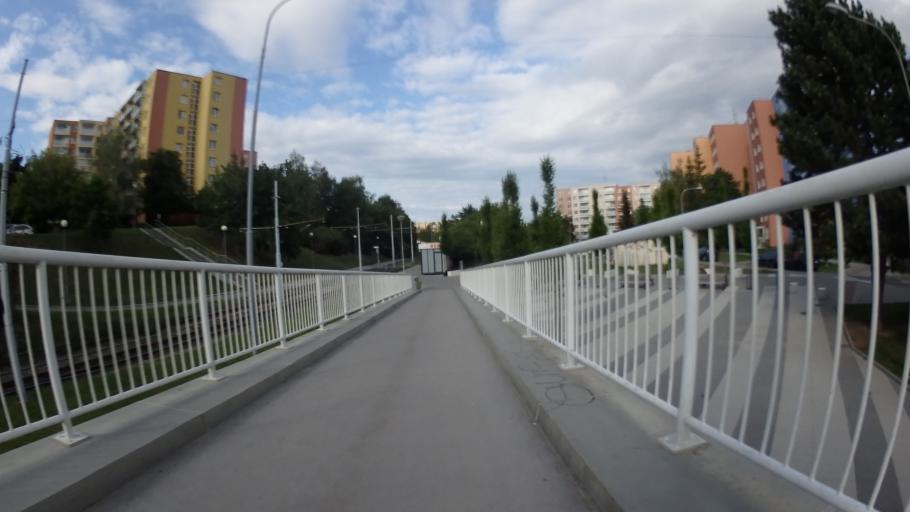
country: CZ
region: South Moravian
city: Moravany
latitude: 49.1688
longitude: 16.5723
